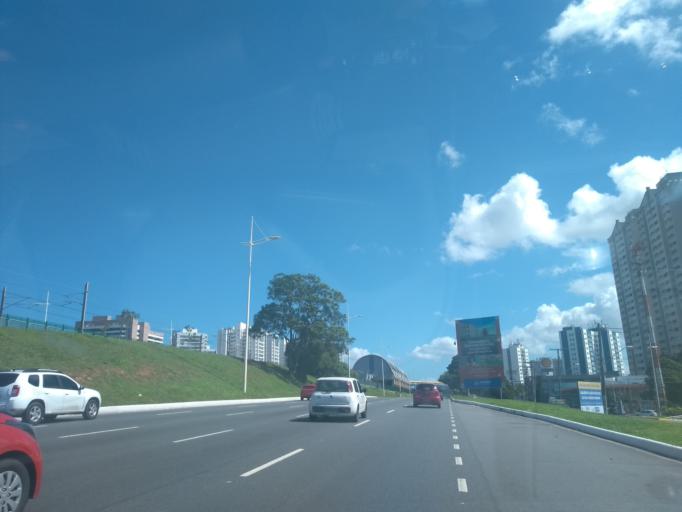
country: BR
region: Bahia
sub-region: Lauro De Freitas
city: Lauro de Freitas
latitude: -12.9371
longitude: -38.4025
